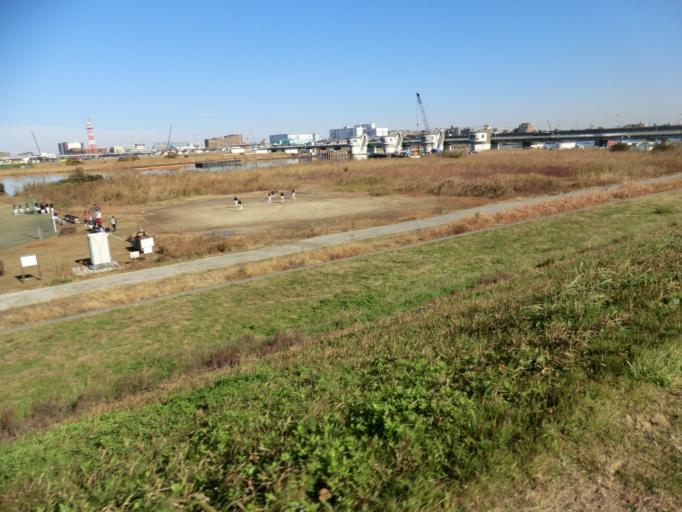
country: JP
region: Tokyo
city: Urayasu
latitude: 35.7022
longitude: 139.9199
